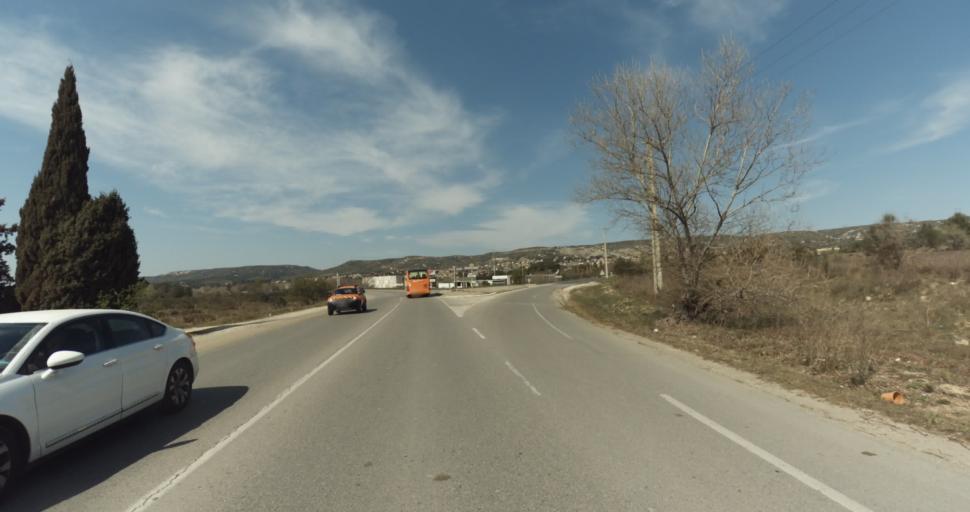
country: FR
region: Provence-Alpes-Cote d'Azur
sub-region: Departement des Bouches-du-Rhone
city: Coudoux
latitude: 43.5446
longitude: 5.2575
